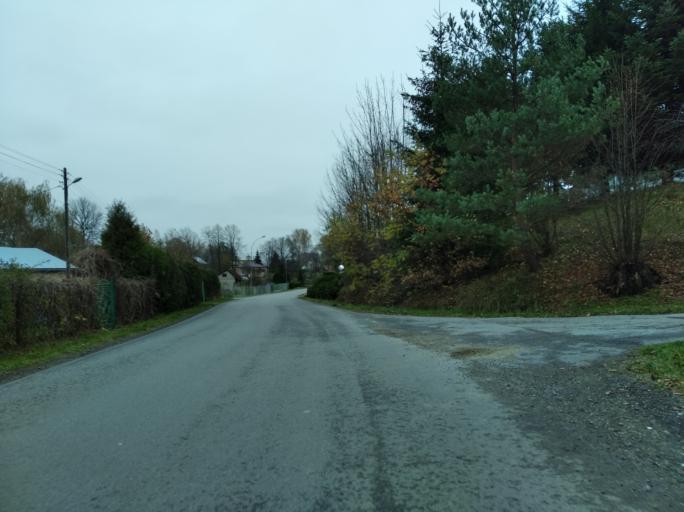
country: PL
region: Subcarpathian Voivodeship
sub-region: Powiat krosnienski
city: Jedlicze
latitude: 49.7348
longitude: 21.6524
